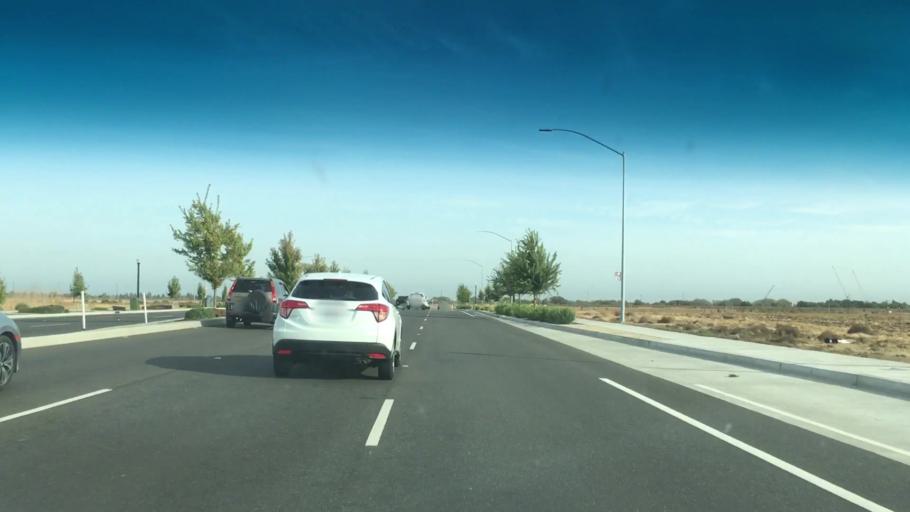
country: US
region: California
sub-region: Sacramento County
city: Parkway
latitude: 38.4651
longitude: -121.4858
